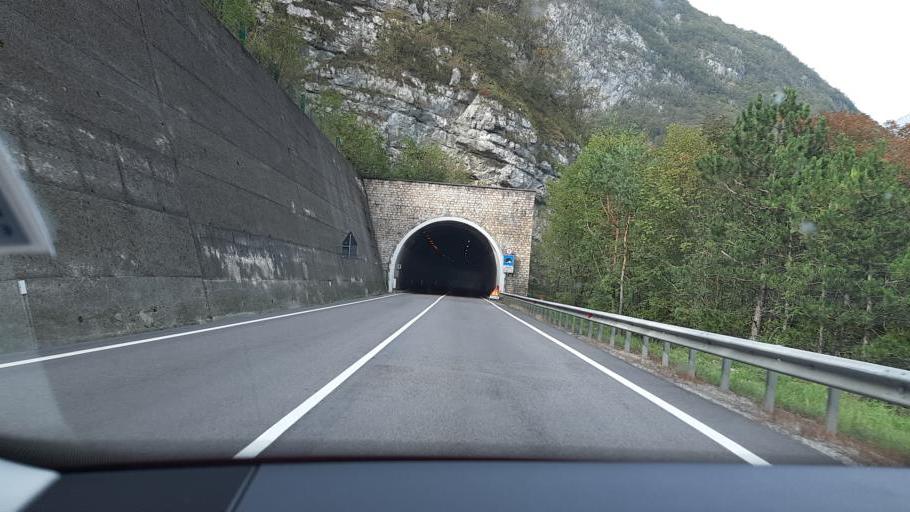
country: IT
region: Trentino-Alto Adige
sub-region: Provincia di Trento
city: Pietramurata
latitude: 46.0524
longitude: 10.9325
